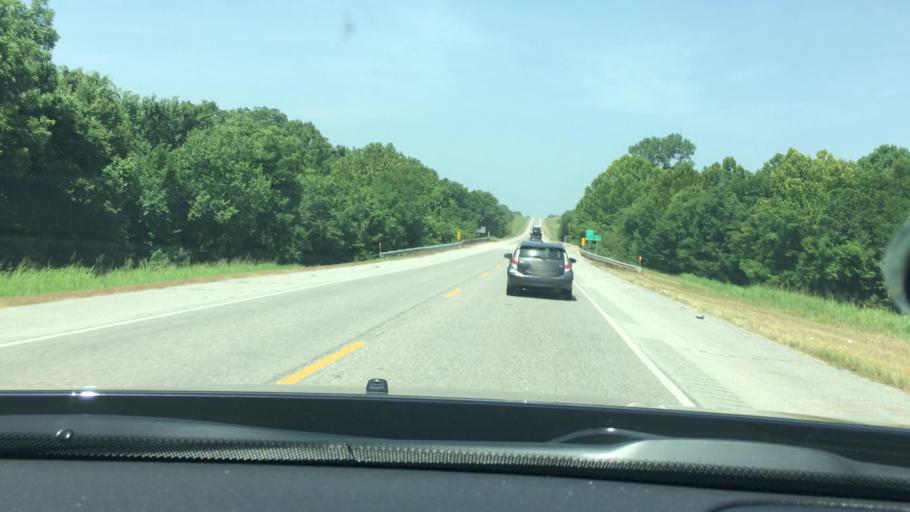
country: US
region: Oklahoma
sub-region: Coal County
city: Coalgate
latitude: 34.6110
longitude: -96.3923
